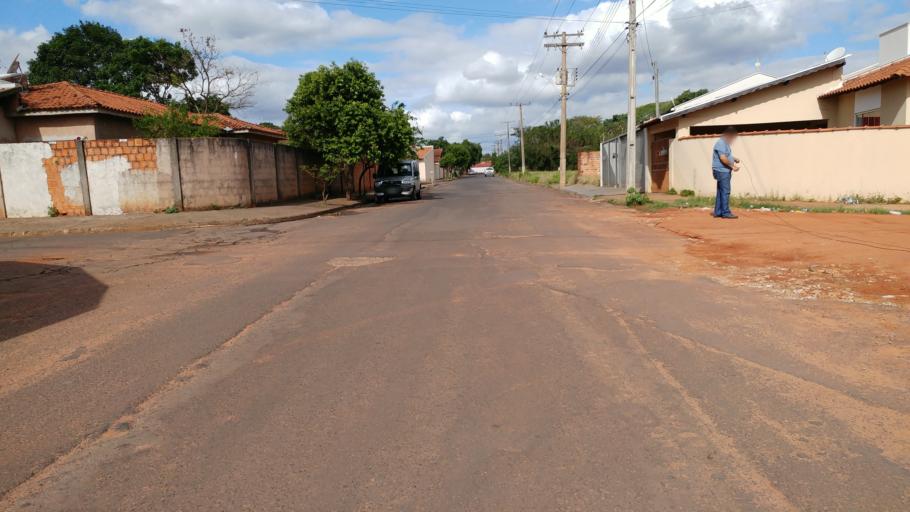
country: BR
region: Sao Paulo
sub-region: Paraguacu Paulista
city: Paraguacu Paulista
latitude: -22.4165
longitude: -50.5900
